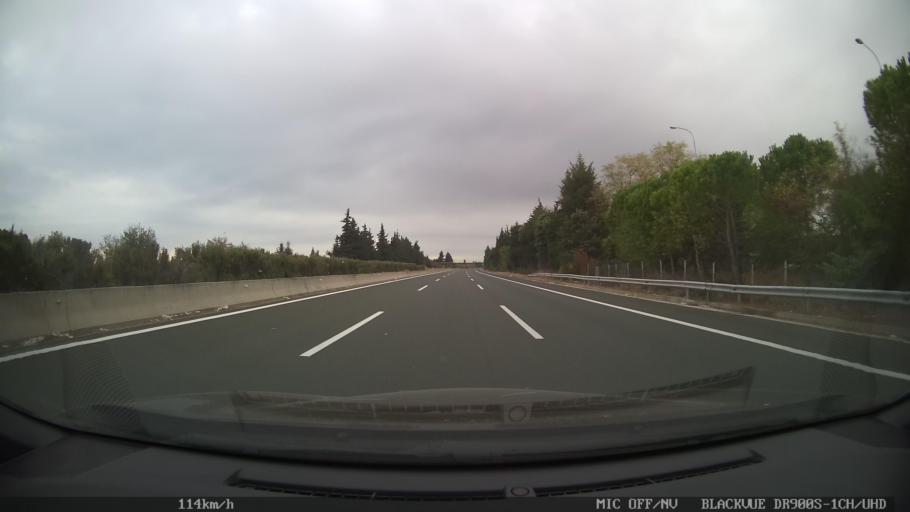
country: GR
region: Central Macedonia
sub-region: Nomos Pierias
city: Makrygialos
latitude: 40.3989
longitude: 22.6002
